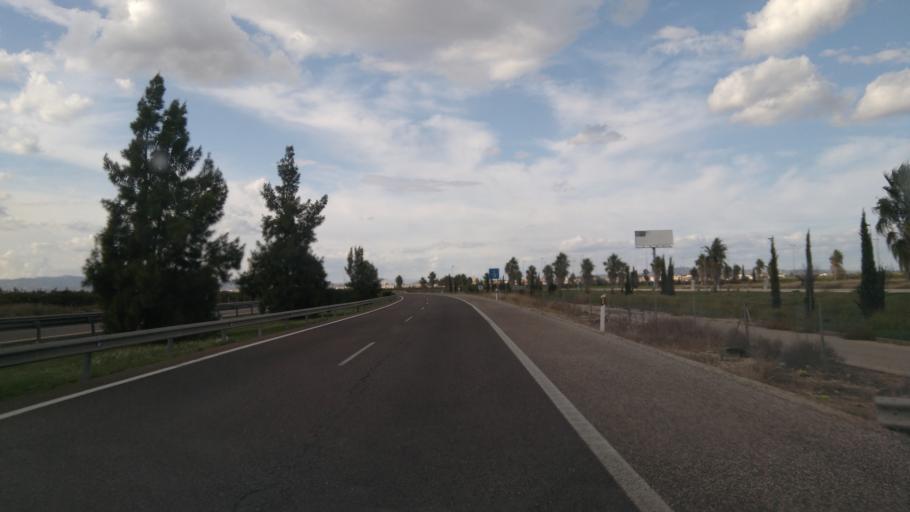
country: ES
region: Valencia
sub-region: Provincia de Valencia
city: Guadassuar
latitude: 39.1730
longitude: -0.4662
